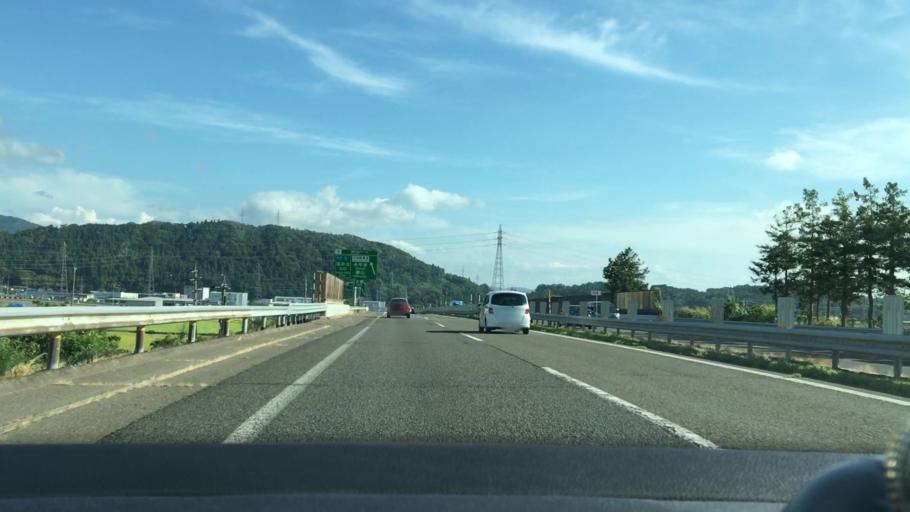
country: JP
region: Fukui
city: Fukui-shi
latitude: 36.0908
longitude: 136.2786
